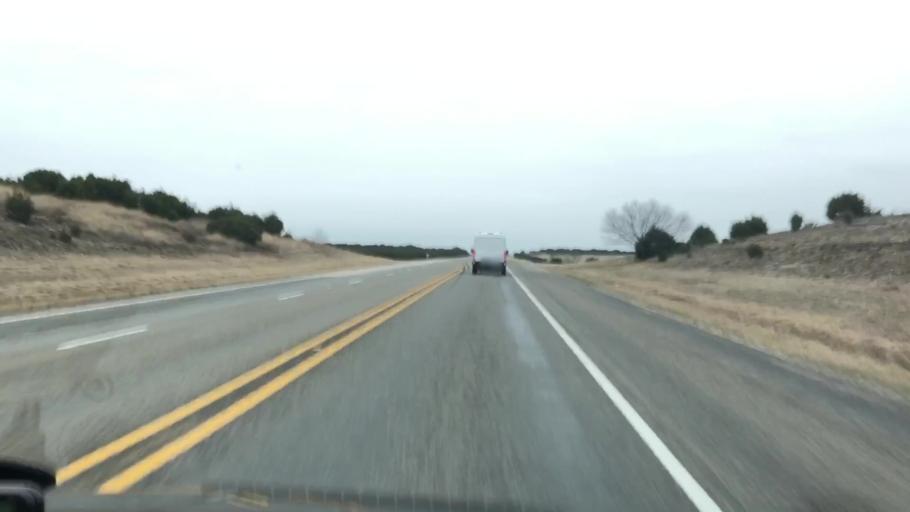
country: US
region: Texas
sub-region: Lampasas County
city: Lampasas
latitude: 31.1448
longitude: -98.1832
